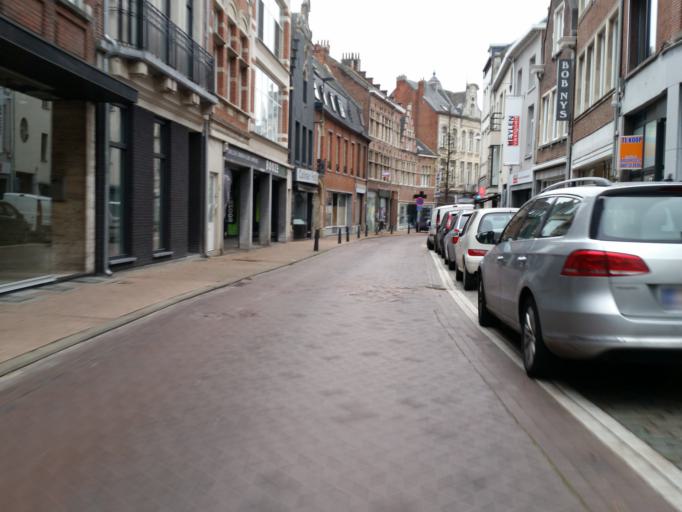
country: BE
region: Flanders
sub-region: Provincie Antwerpen
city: Lier
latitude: 51.1287
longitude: 4.5787
